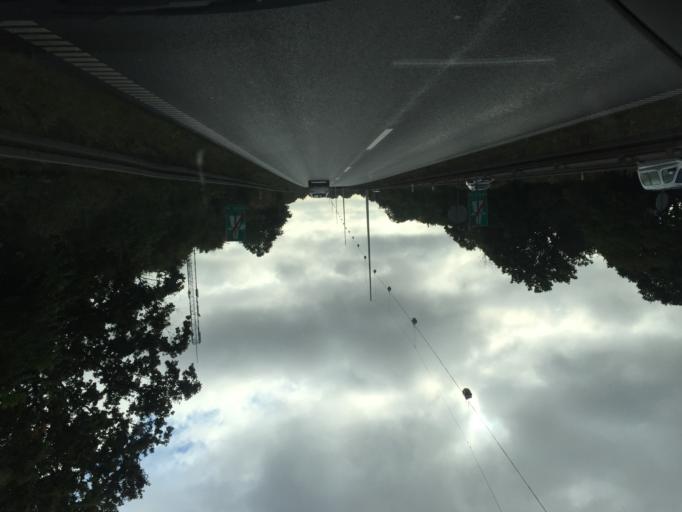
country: DK
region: Capital Region
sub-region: Gladsaxe Municipality
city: Buddinge
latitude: 55.7215
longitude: 12.4927
